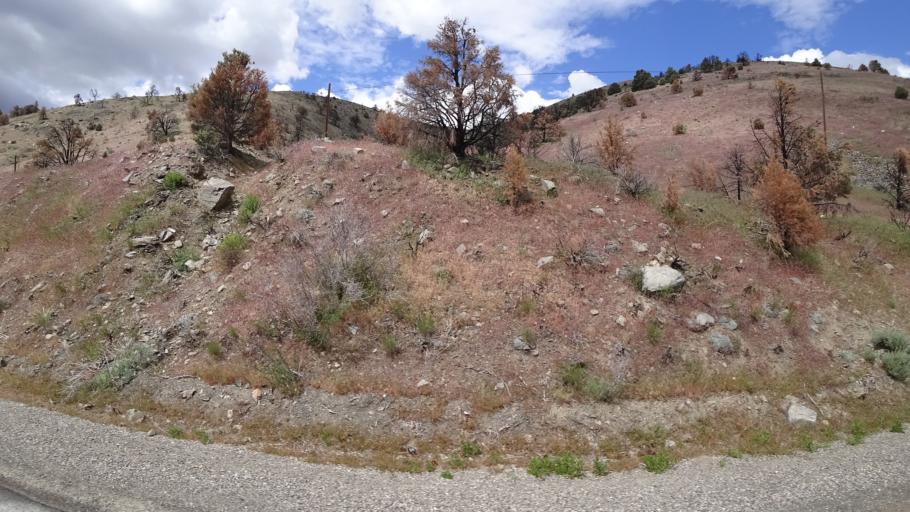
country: US
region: Nevada
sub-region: Lyon County
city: Smith Valley
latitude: 38.6838
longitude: -119.5485
